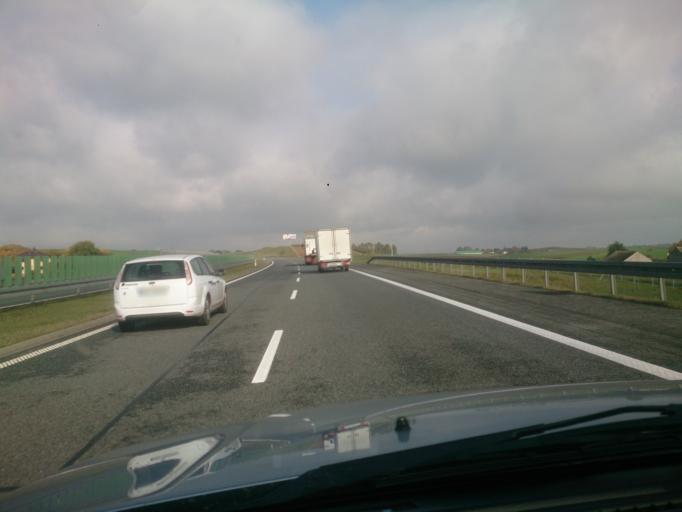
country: PL
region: Pomeranian Voivodeship
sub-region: Powiat starogardzki
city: Bobowo
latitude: 53.8592
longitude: 18.6307
